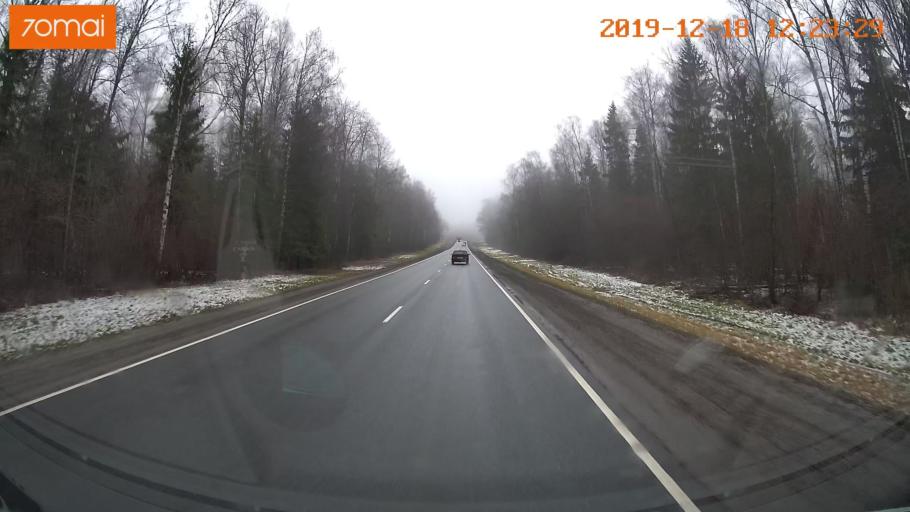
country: RU
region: Moskovskaya
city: Novopetrovskoye
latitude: 56.0138
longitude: 36.4934
